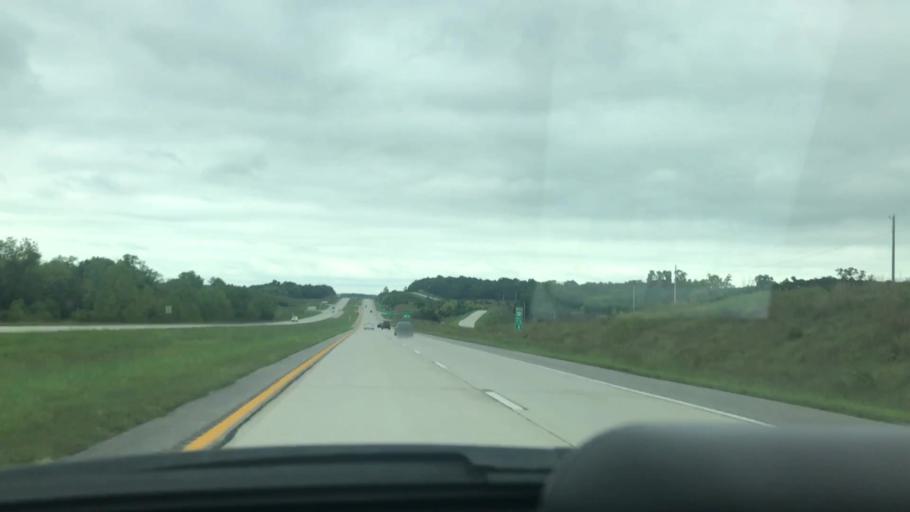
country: US
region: Missouri
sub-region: Greene County
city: Fair Grove
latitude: 37.5115
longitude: -93.1387
